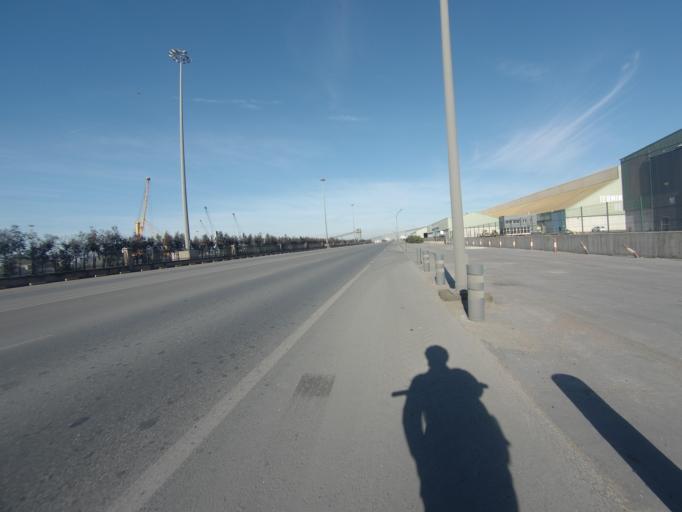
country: ES
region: Andalusia
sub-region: Provincia de Huelva
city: Punta Umbria
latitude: 37.1935
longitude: -6.9317
